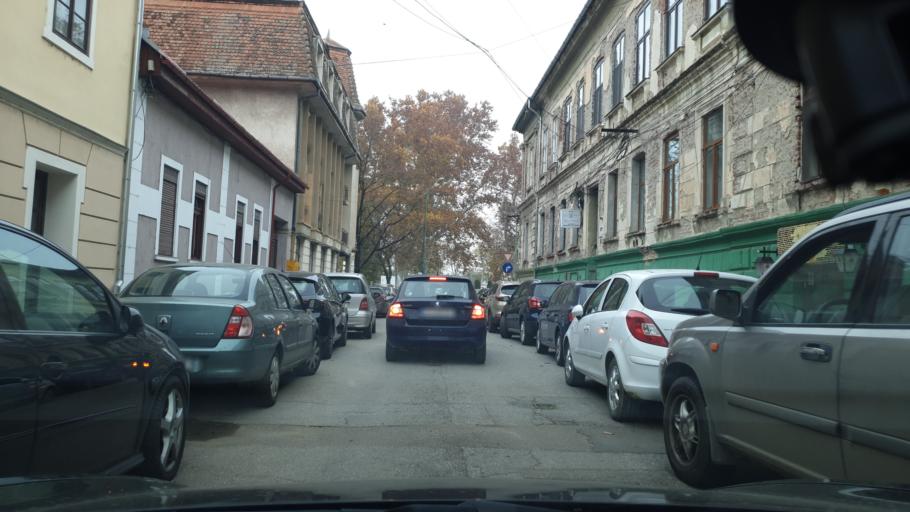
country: RO
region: Timis
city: Timisoara
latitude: 45.7586
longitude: 21.2309
